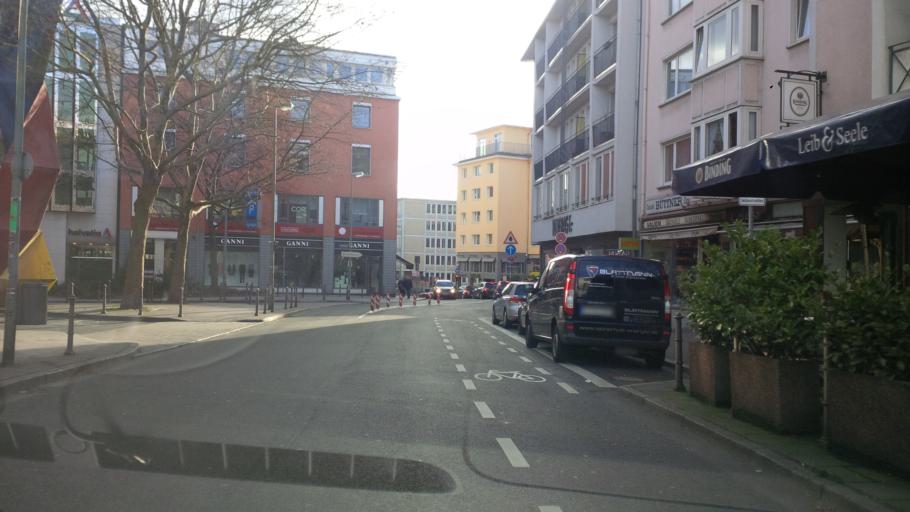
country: DE
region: Hesse
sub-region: Regierungsbezirk Darmstadt
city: Frankfurt am Main
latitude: 50.1122
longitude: 8.6795
